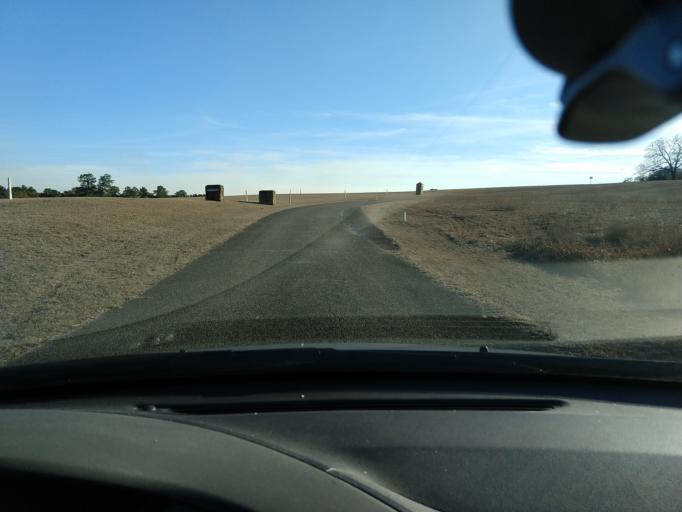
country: US
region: Georgia
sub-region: Macon County
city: Oglethorpe
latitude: 32.1937
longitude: -84.1309
